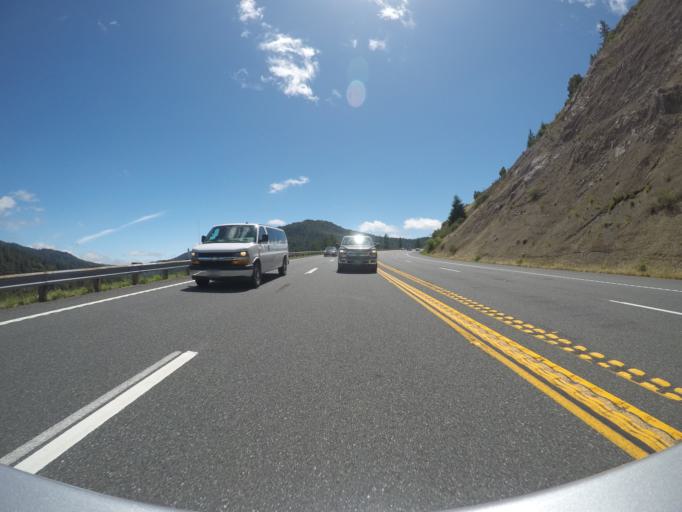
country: US
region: California
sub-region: Mendocino County
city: Laytonville
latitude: 39.8297
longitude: -123.6520
